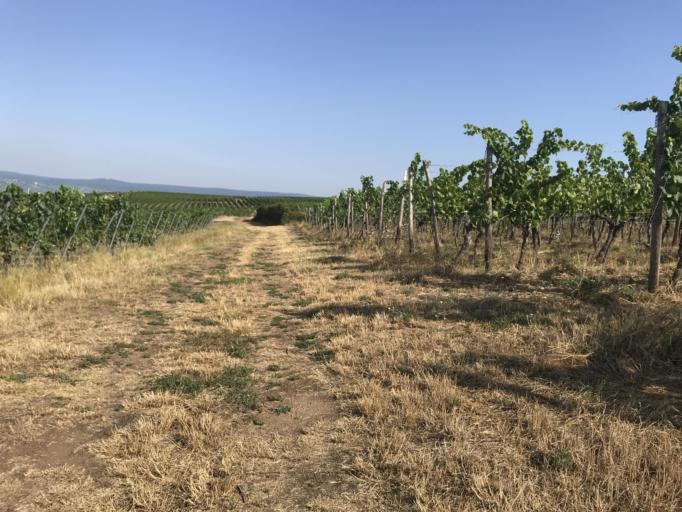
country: DE
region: Rheinland-Pfalz
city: Nieder-Ingelheim
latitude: 49.9564
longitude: 8.0747
